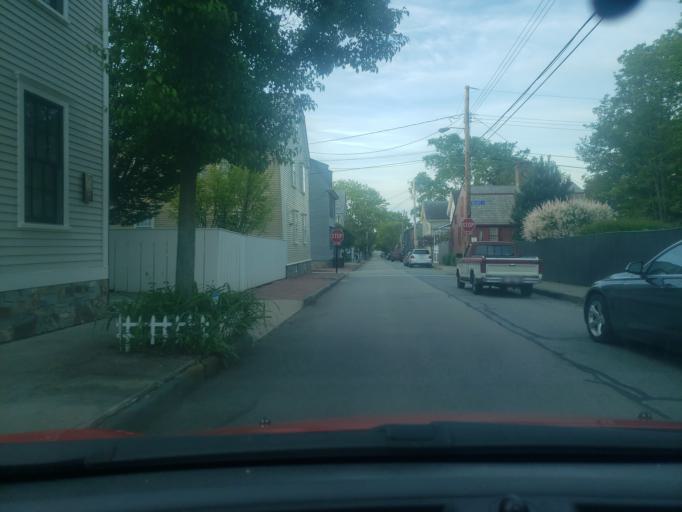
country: US
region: Rhode Island
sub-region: Newport County
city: Newport
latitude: 41.4950
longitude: -71.3199
